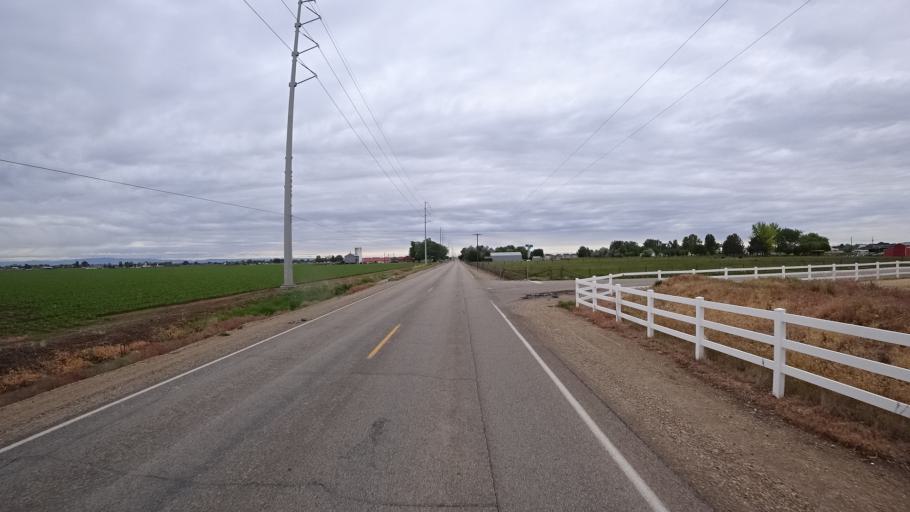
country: US
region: Idaho
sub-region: Ada County
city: Meridian
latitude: 43.6486
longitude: -116.4446
